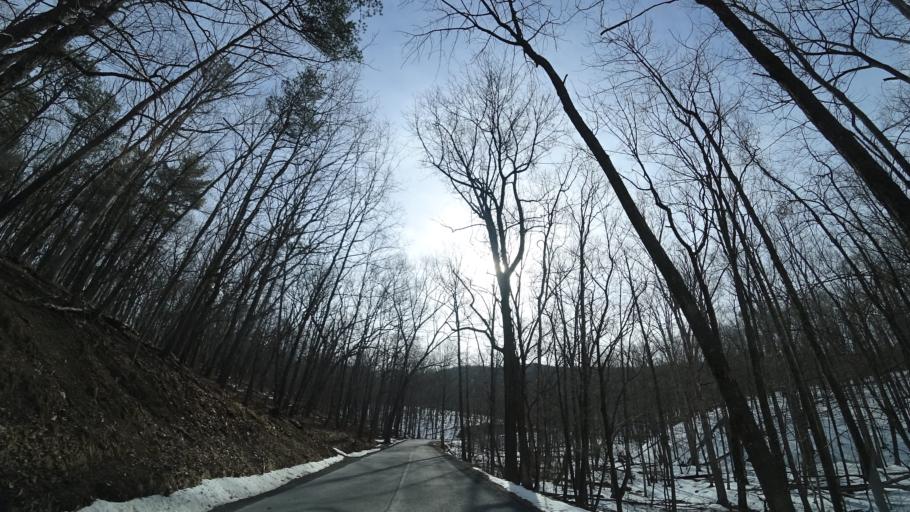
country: US
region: Virginia
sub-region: Shenandoah County
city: Basye
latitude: 38.9330
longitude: -78.6899
